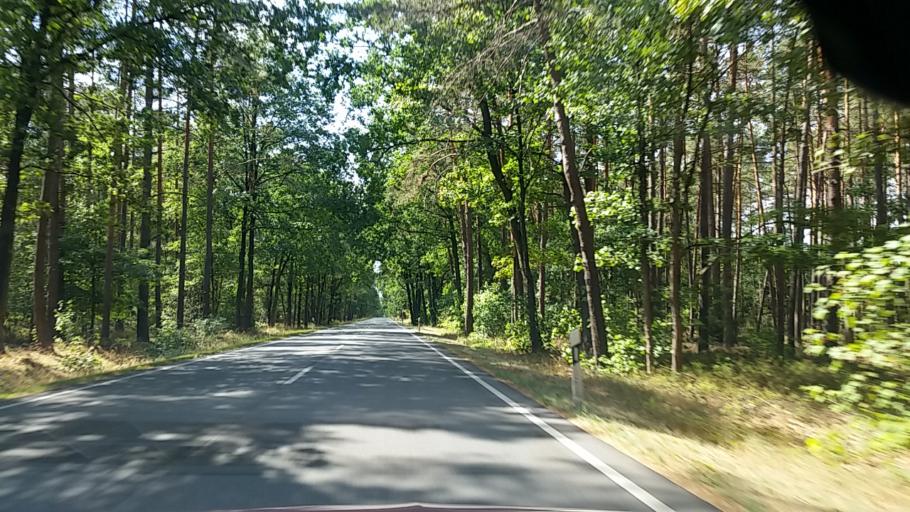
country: DE
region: Lower Saxony
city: Hankensbuttel
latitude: 52.7170
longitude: 10.5714
